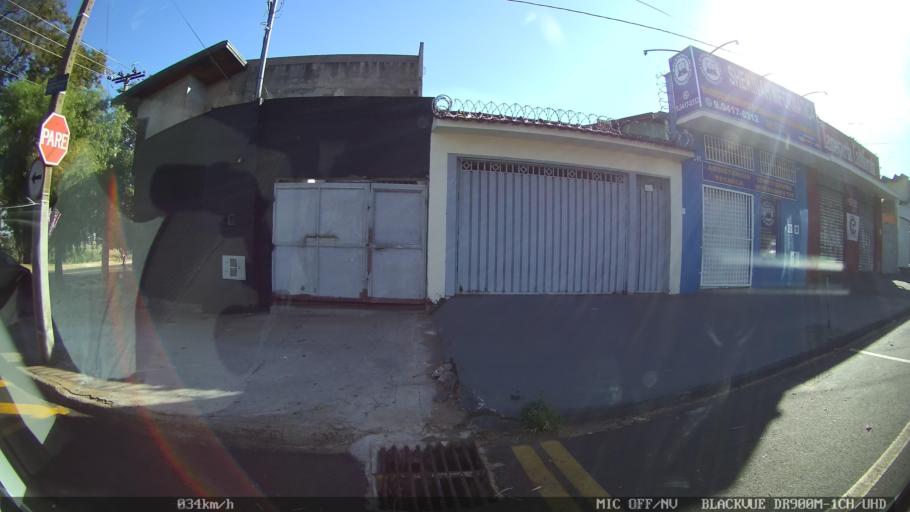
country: BR
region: Sao Paulo
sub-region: Franca
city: Franca
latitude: -20.5088
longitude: -47.4153
